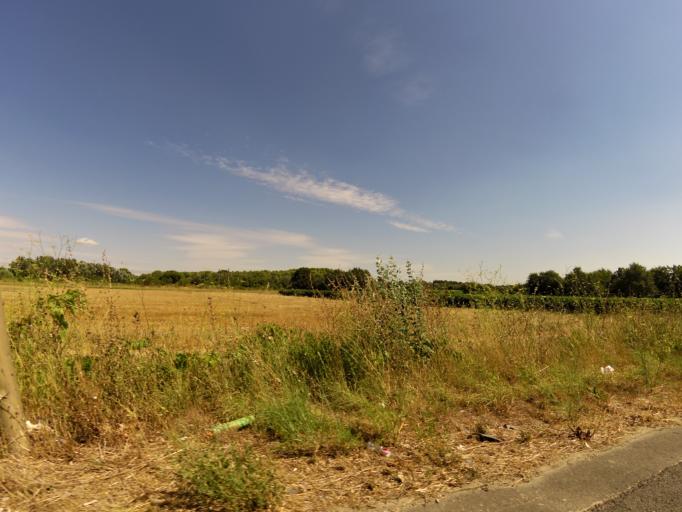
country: FR
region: Languedoc-Roussillon
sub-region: Departement de l'Herault
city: Valergues
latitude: 43.6746
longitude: 4.0696
